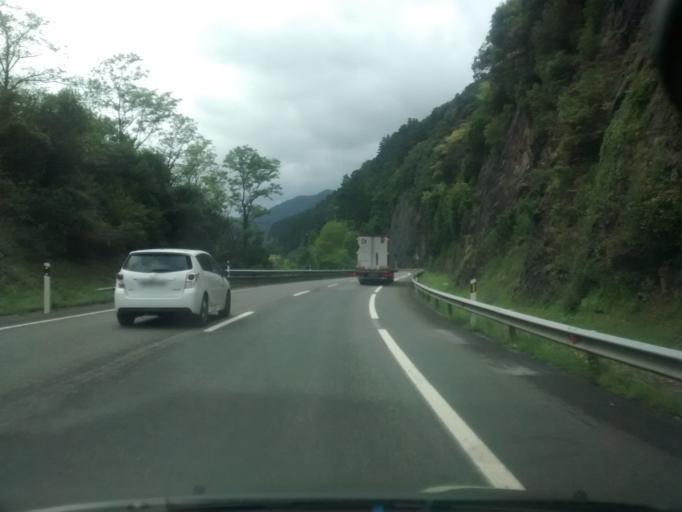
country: ES
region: Basque Country
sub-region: Provincia de Guipuzcoa
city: Mendaro
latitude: 43.2653
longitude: -2.3751
